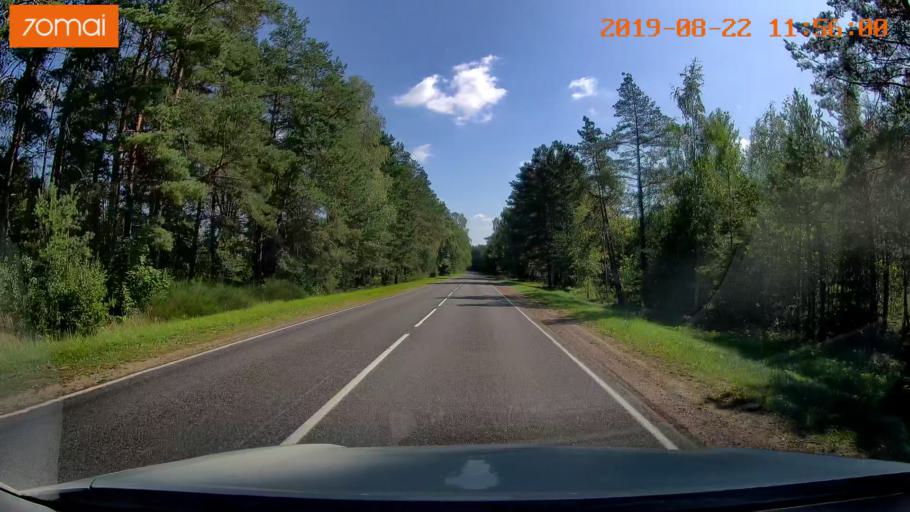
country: BY
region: Minsk
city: Prawdzinski
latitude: 53.4296
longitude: 27.5608
